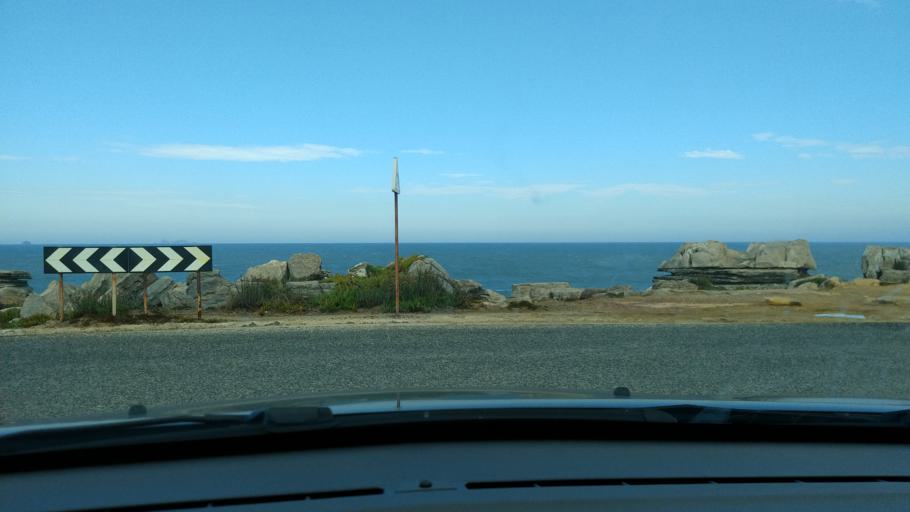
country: PT
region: Leiria
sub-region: Peniche
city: Peniche
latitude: 39.3672
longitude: -9.4021
